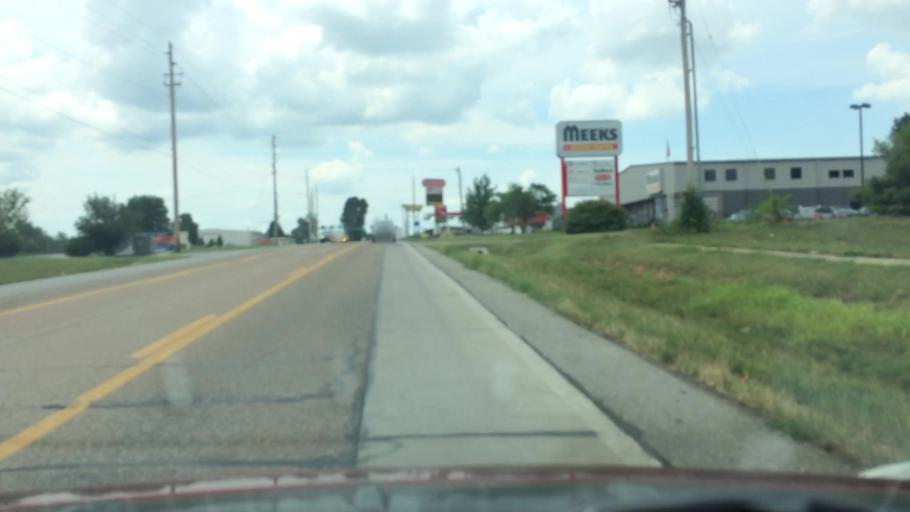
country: US
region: Missouri
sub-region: Greene County
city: Springfield
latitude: 37.2566
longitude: -93.2651
